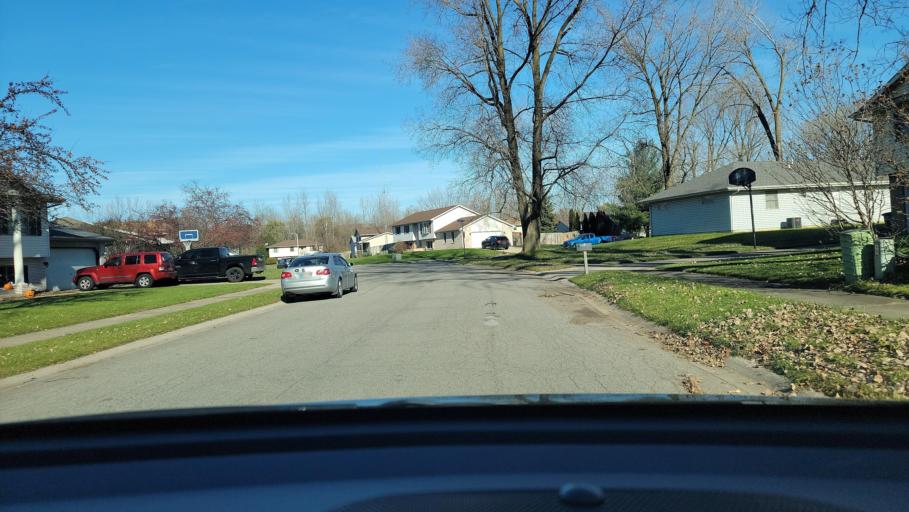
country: US
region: Indiana
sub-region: Porter County
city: Portage
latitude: 41.5879
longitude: -87.1957
